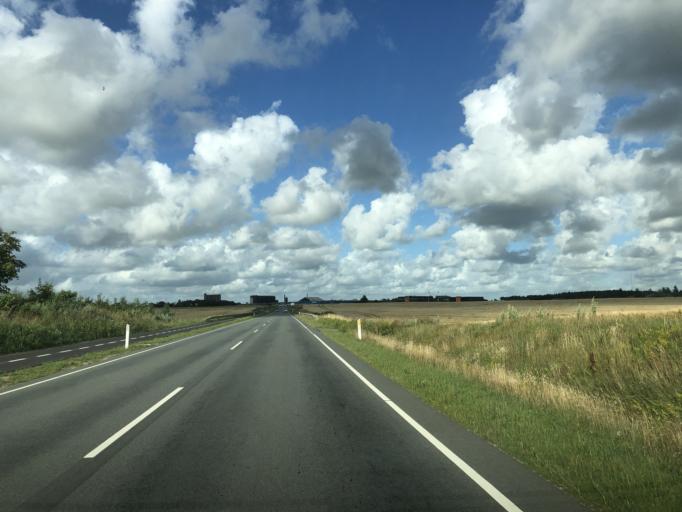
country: DK
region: Central Jutland
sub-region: Lemvig Kommune
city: Lemvig
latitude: 56.5108
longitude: 8.2967
